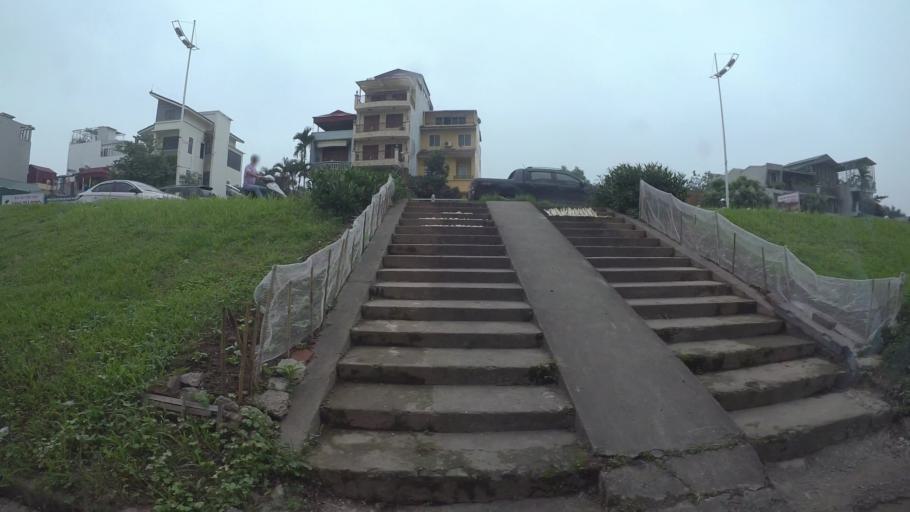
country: VN
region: Ha Noi
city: Tay Ho
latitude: 21.0726
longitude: 105.8256
